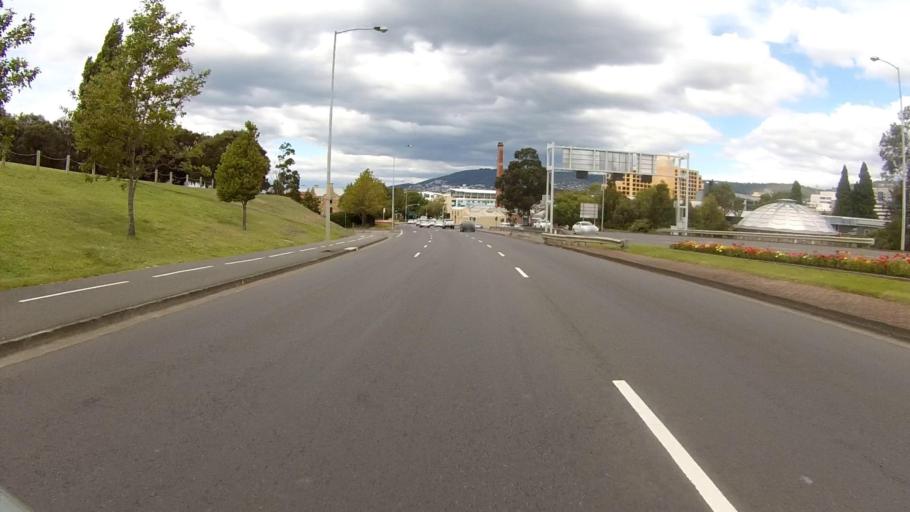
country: AU
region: Tasmania
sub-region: Hobart
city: Hobart
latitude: -42.8776
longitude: 147.3342
